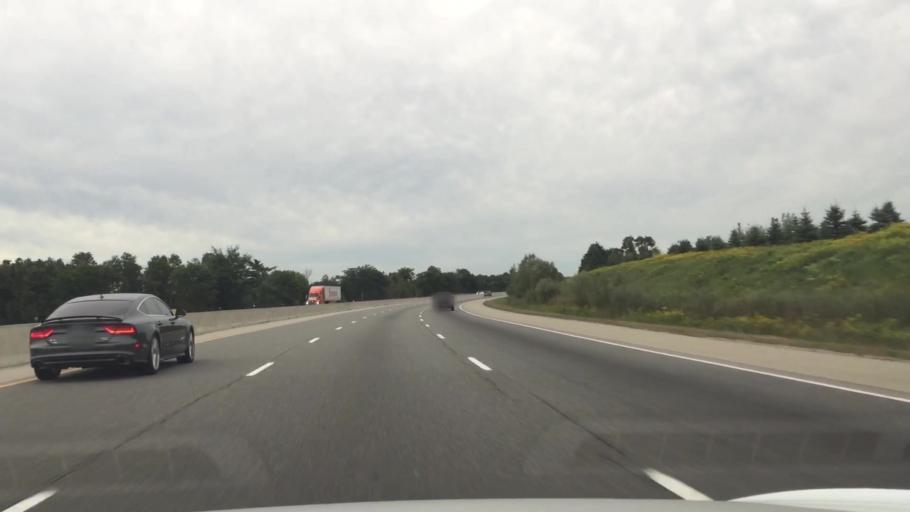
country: CA
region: Ontario
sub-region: Oxford County
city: Woodstock
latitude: 43.2120
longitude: -80.6094
